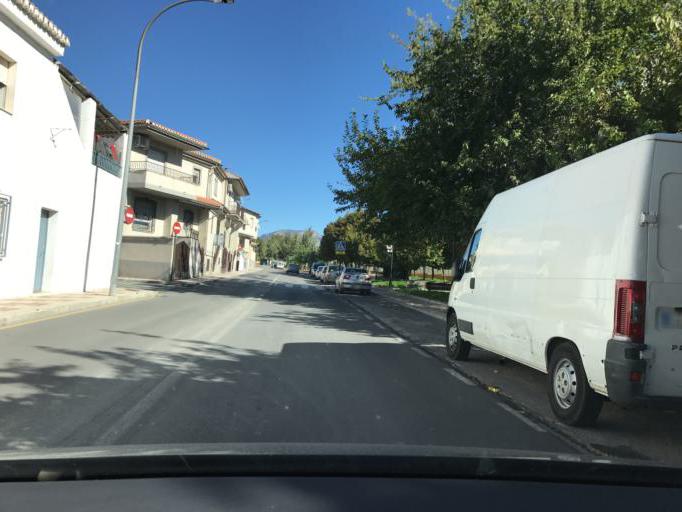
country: ES
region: Andalusia
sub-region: Provincia de Granada
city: Maracena
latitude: 37.2019
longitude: -3.6331
